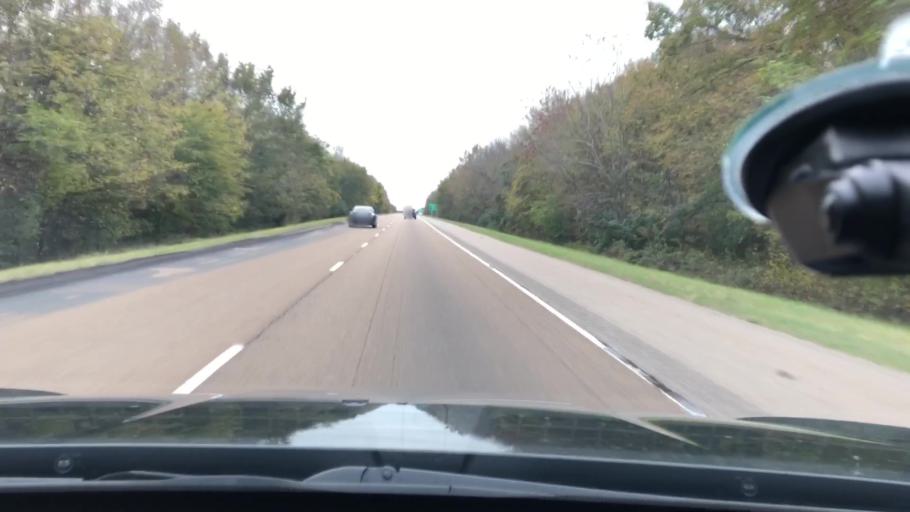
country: US
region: Arkansas
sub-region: Nevada County
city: Prescott
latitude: 33.8040
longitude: -93.4320
